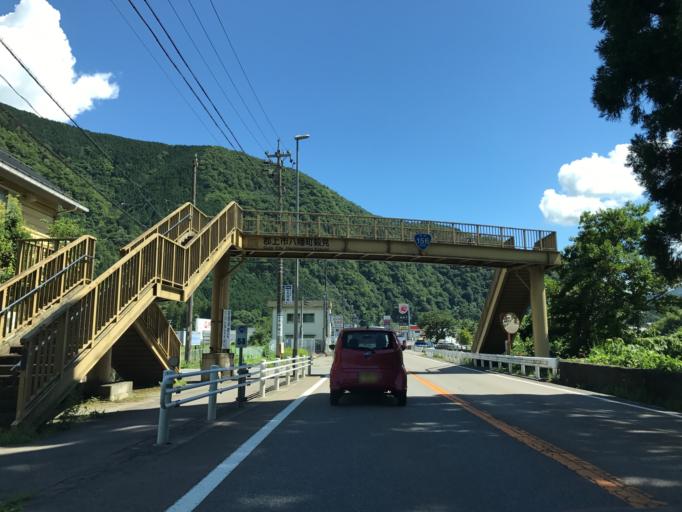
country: JP
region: Gifu
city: Gujo
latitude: 35.7340
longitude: 136.9534
